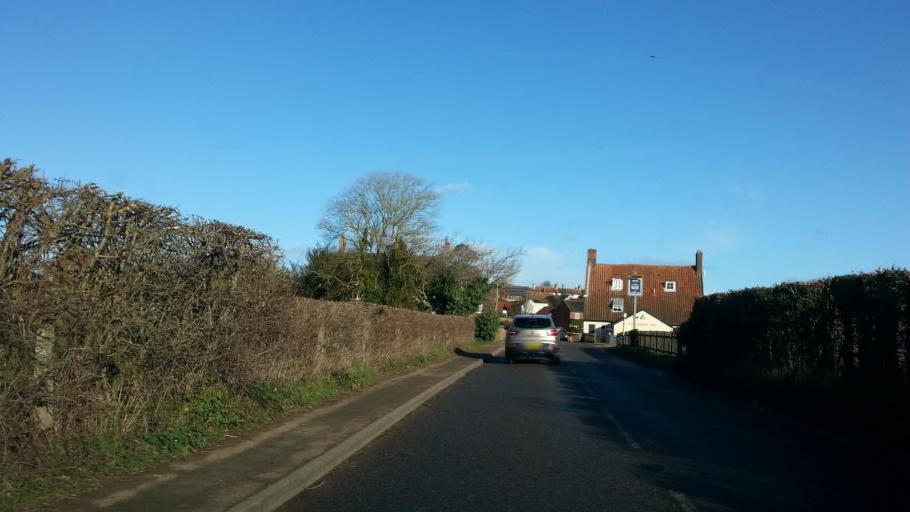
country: GB
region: England
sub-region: Suffolk
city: Saxmundham
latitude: 52.1682
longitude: 1.4988
